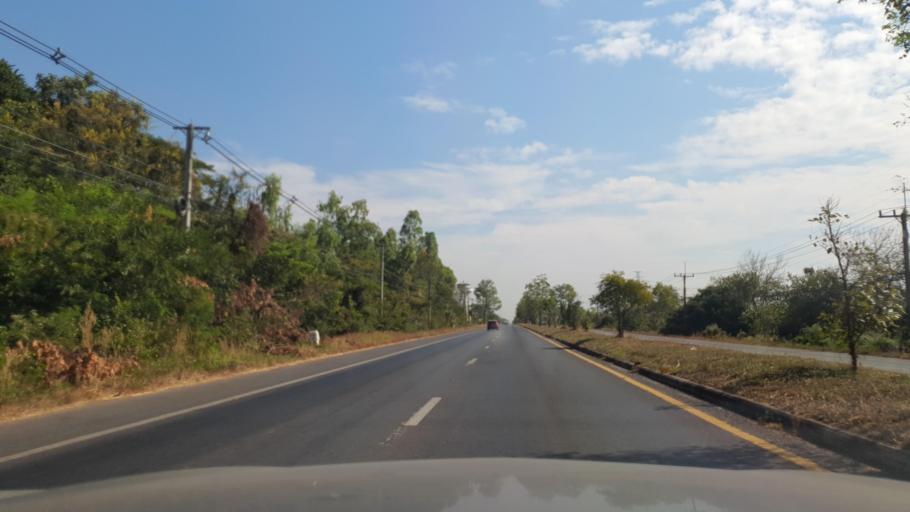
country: TH
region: Maha Sarakham
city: Kantharawichai
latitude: 16.3880
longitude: 103.2545
